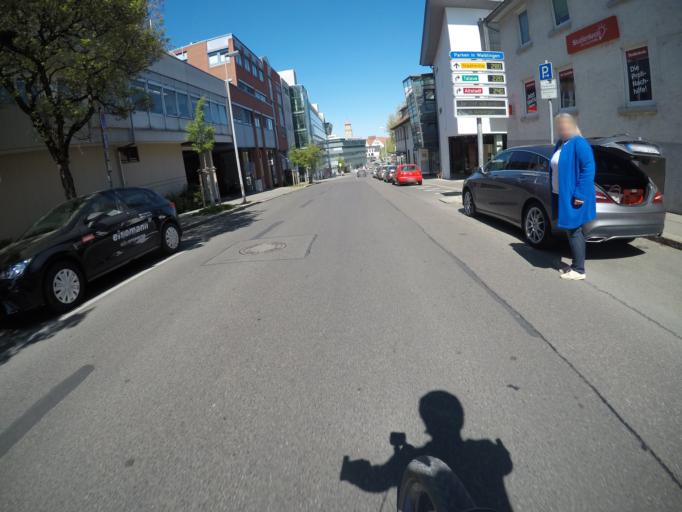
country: DE
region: Baden-Wuerttemberg
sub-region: Regierungsbezirk Stuttgart
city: Waiblingen
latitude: 48.8286
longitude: 9.3149
